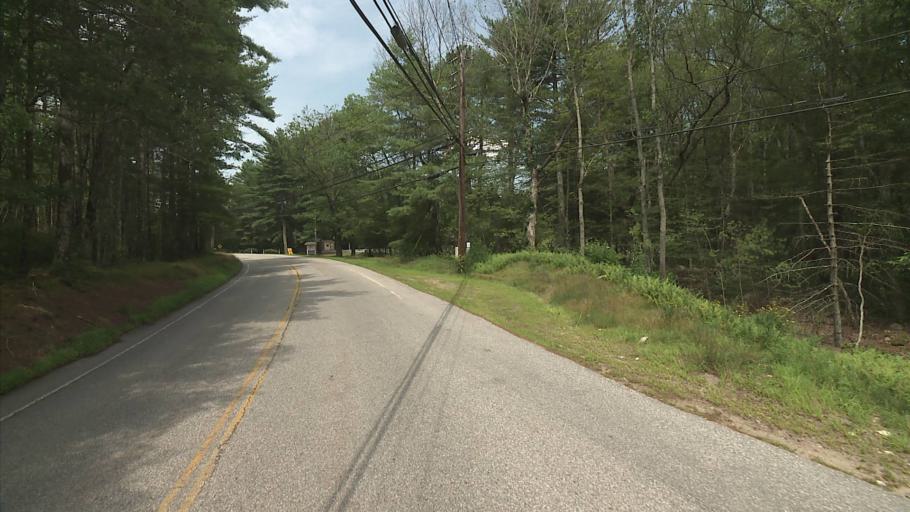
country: US
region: Connecticut
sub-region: Windham County
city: Danielson
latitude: 41.8015
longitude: -71.8526
